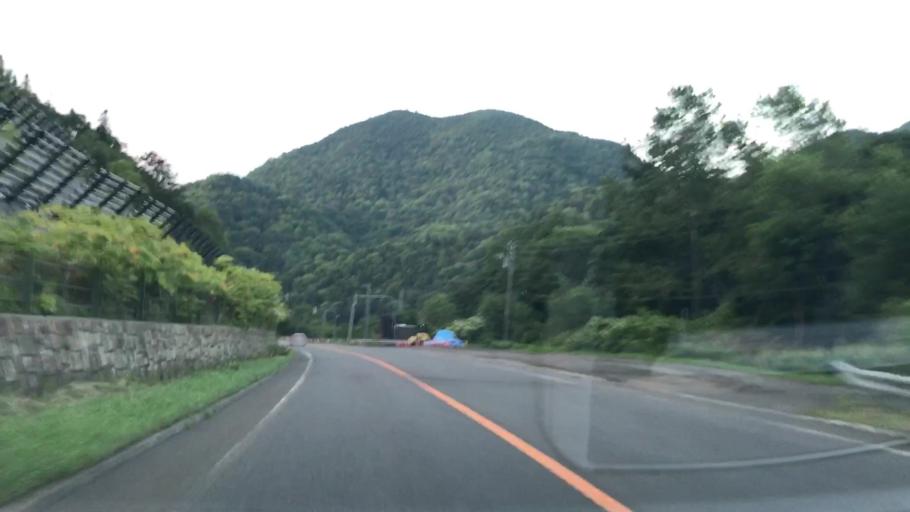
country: JP
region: Hokkaido
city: Sapporo
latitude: 42.9156
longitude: 141.1239
